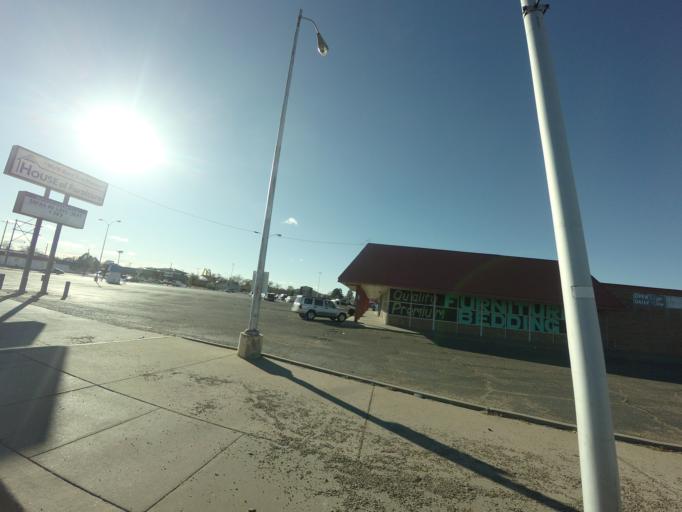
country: US
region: New Mexico
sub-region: Curry County
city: Clovis
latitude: 34.4127
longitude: -103.2054
